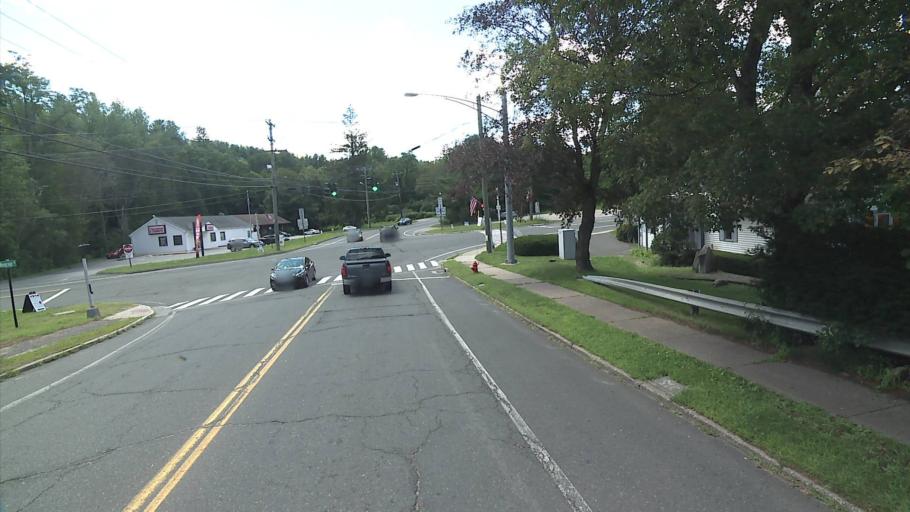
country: US
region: Connecticut
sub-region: Litchfield County
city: New Hartford Center
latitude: 41.8779
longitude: -72.9778
